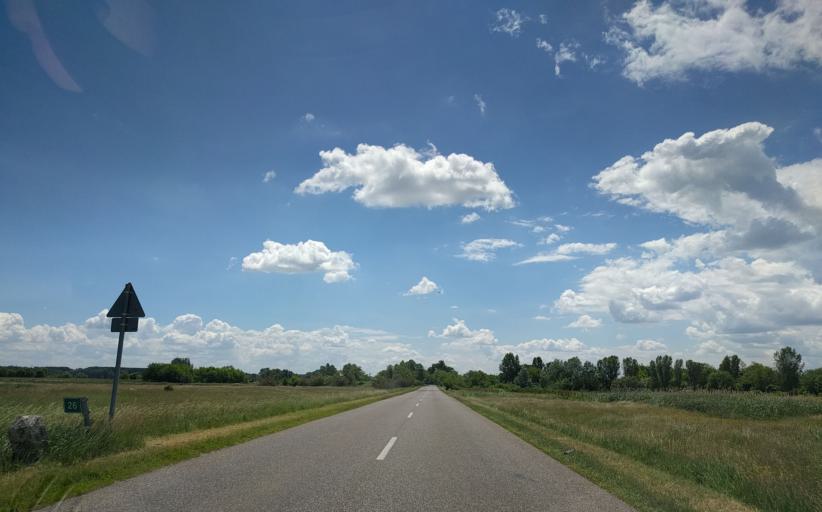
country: HU
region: Bacs-Kiskun
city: Tiszakecske
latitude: 46.9980
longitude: 20.1253
